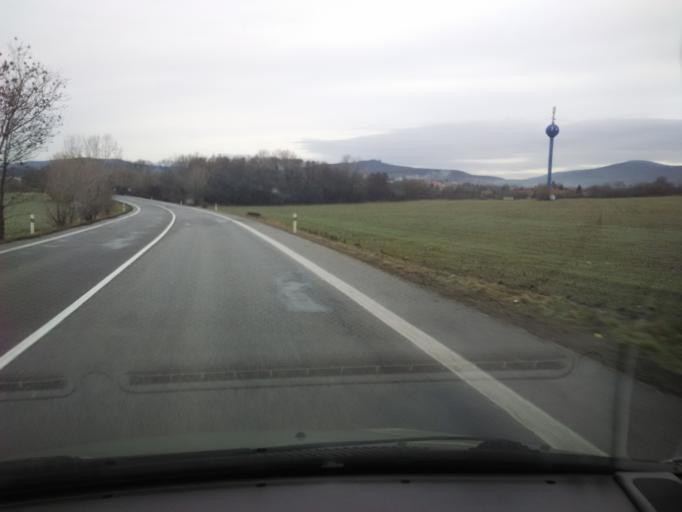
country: SK
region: Nitriansky
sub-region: Okres Nitra
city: Vrable
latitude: 48.3607
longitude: 18.2794
